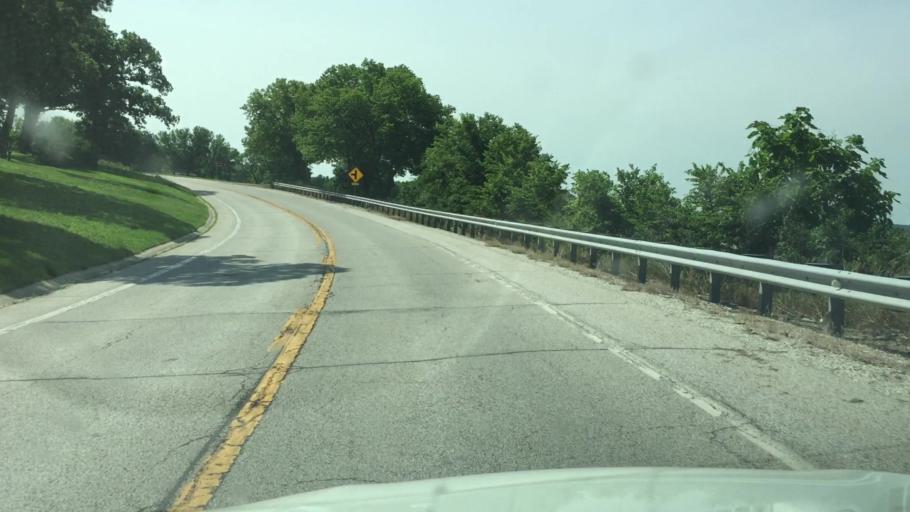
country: US
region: Illinois
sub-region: Hancock County
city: Nauvoo
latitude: 40.5208
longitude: -91.3646
